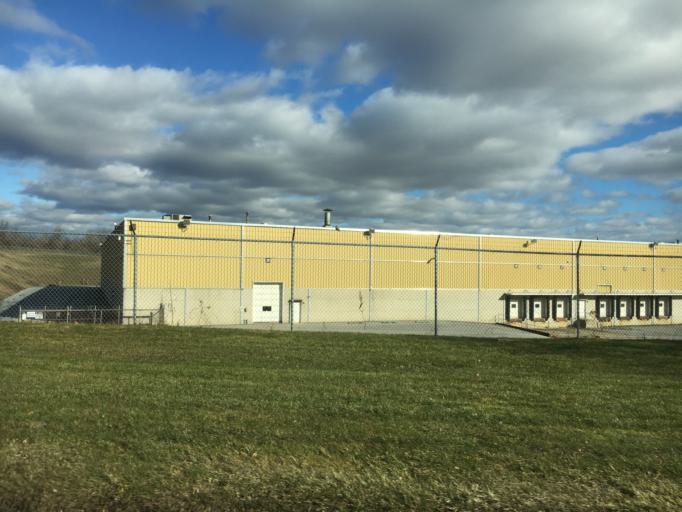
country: US
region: Pennsylvania
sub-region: Lehigh County
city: Stiles
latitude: 40.6644
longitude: -75.5193
